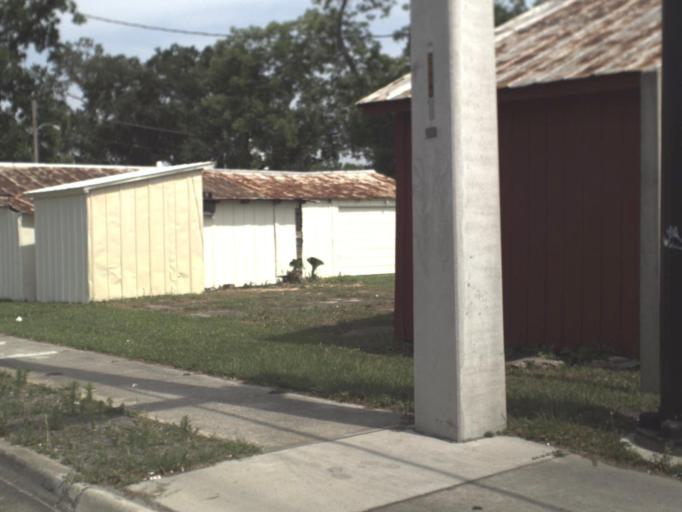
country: US
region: Florida
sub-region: Clay County
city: Bellair-Meadowbrook Terrace
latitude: 30.2483
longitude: -81.7388
